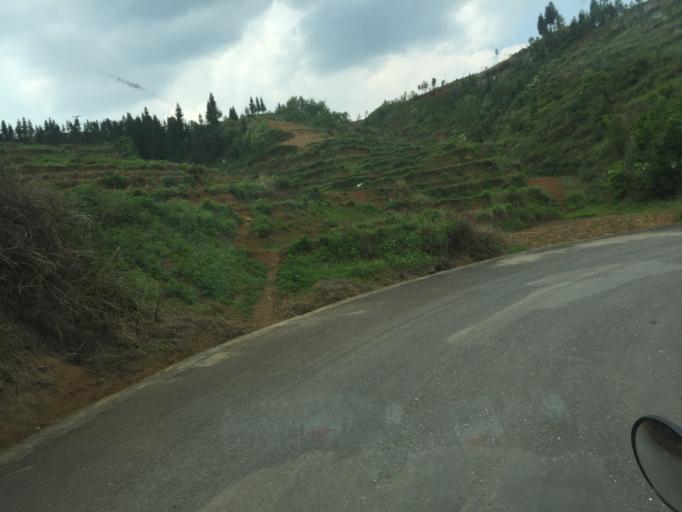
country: CN
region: Guangxi Zhuangzu Zizhiqu
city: Xinzhou
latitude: 25.6604
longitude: 105.2369
